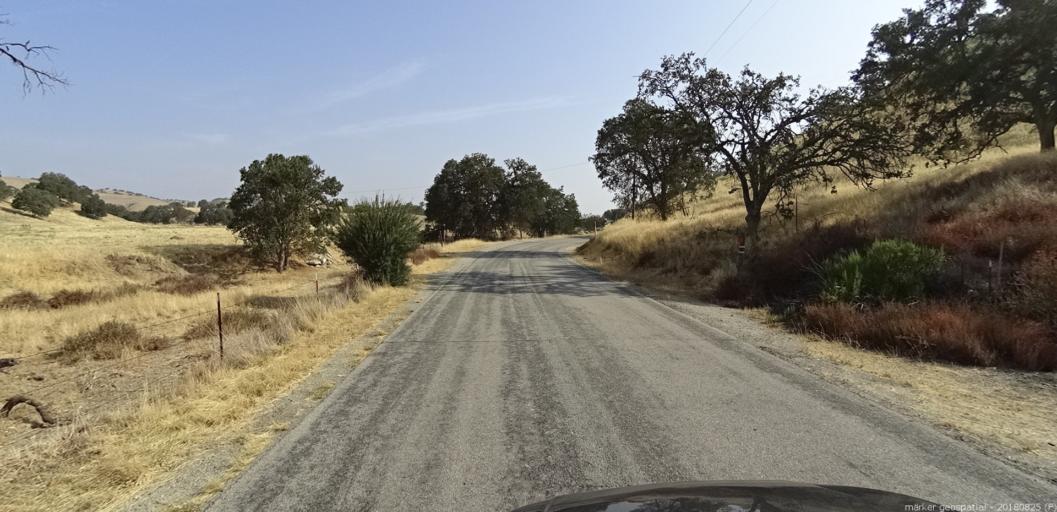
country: US
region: California
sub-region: San Luis Obispo County
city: San Miguel
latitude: 35.7499
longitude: -120.6115
